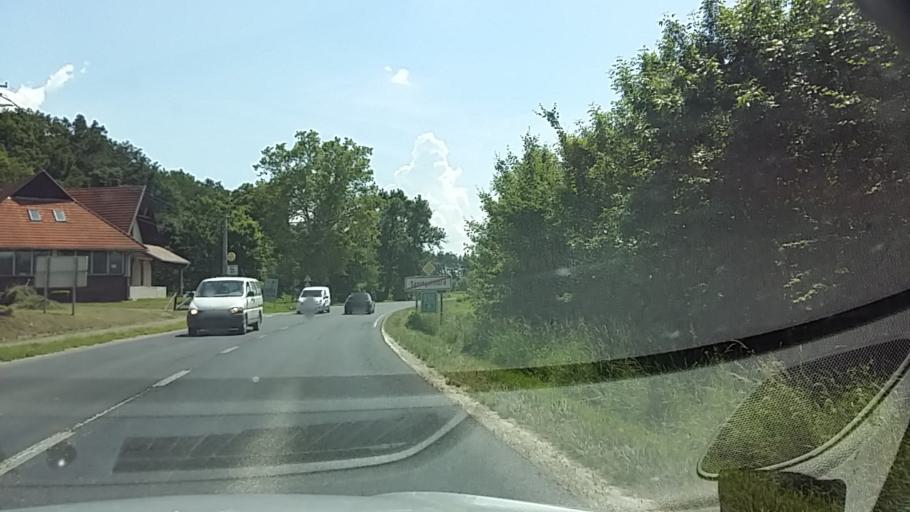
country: AT
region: Burgenland
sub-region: Politischer Bezirk Gussing
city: Inzenhof
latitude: 46.9790
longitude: 16.3291
